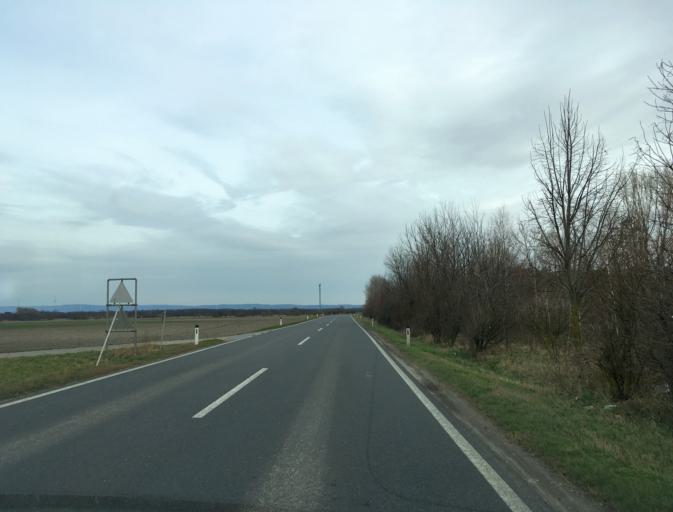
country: AT
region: Lower Austria
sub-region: Politischer Bezirk Ganserndorf
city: Lassee
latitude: 48.2248
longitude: 16.8458
